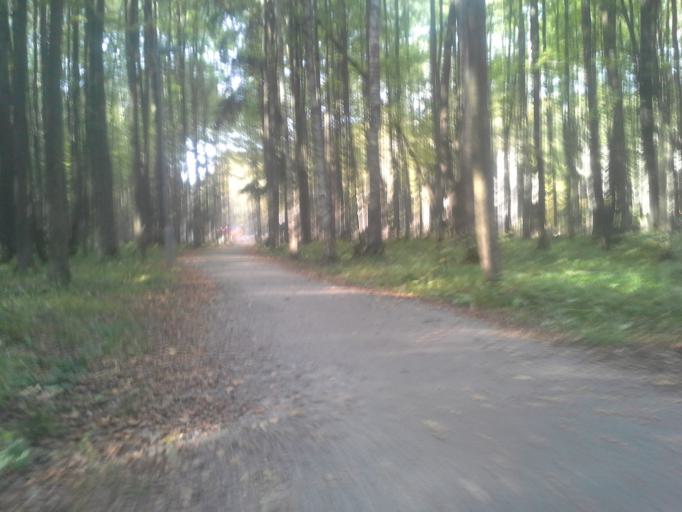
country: RU
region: Moskovskaya
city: Kievskij
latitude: 55.4264
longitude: 36.8771
